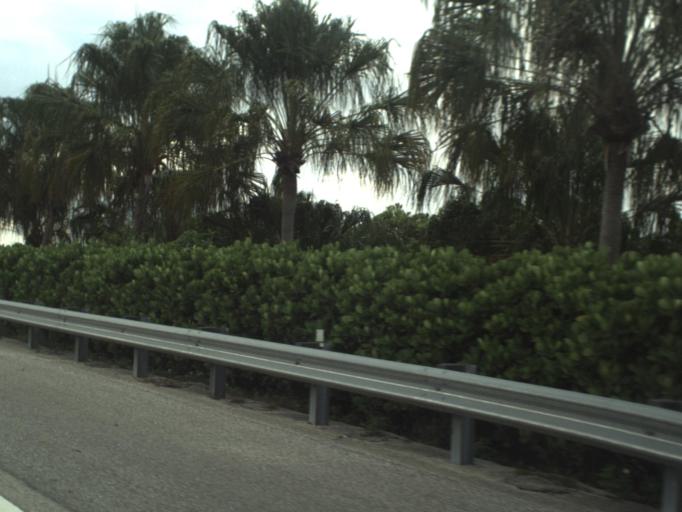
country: US
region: Florida
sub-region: Miami-Dade County
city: Glenvar Heights
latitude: 25.6958
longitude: -80.3323
